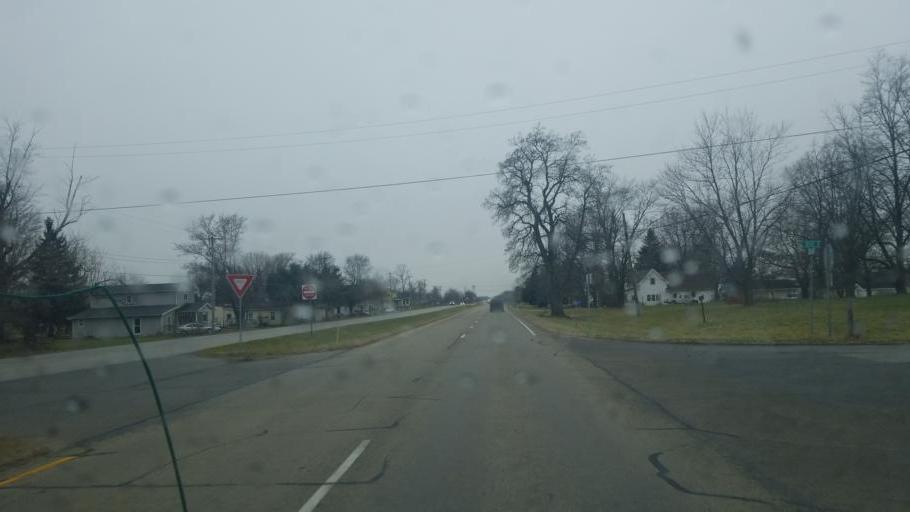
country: US
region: Indiana
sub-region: Henry County
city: Knightstown
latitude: 39.7905
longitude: -85.6445
